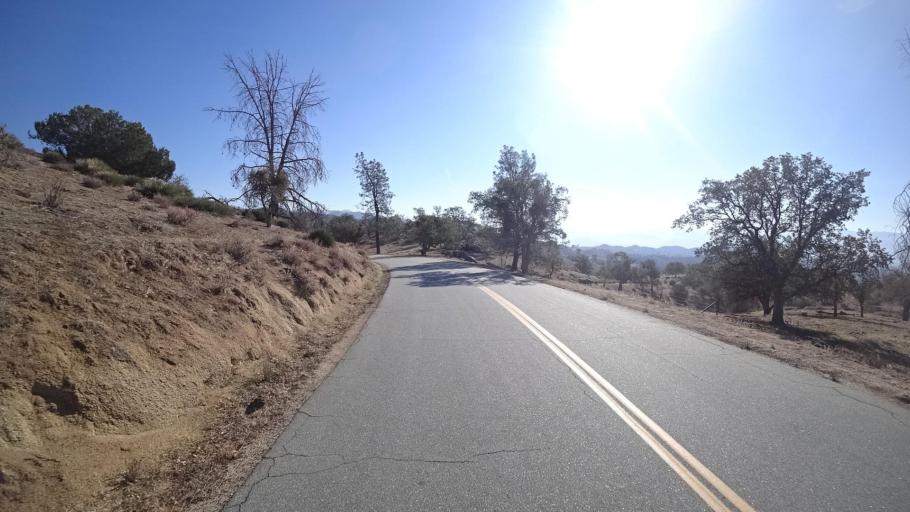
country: US
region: California
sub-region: Kern County
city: Bodfish
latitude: 35.3808
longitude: -118.4061
